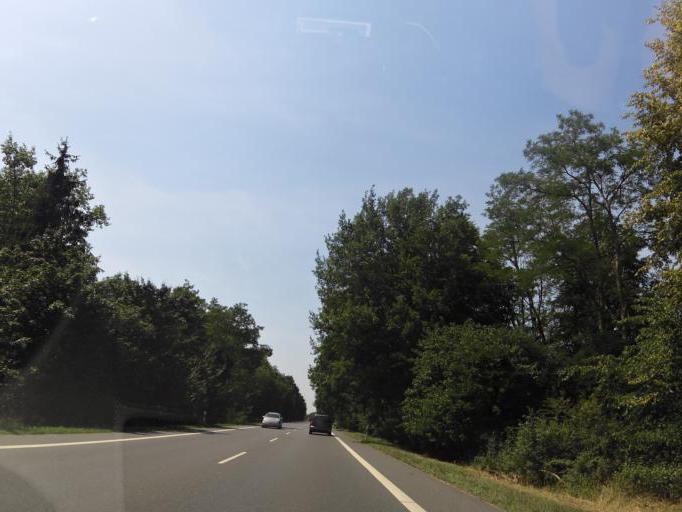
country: DE
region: Hesse
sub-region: Regierungsbezirk Darmstadt
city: Buttelborn
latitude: 49.9045
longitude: 8.5493
